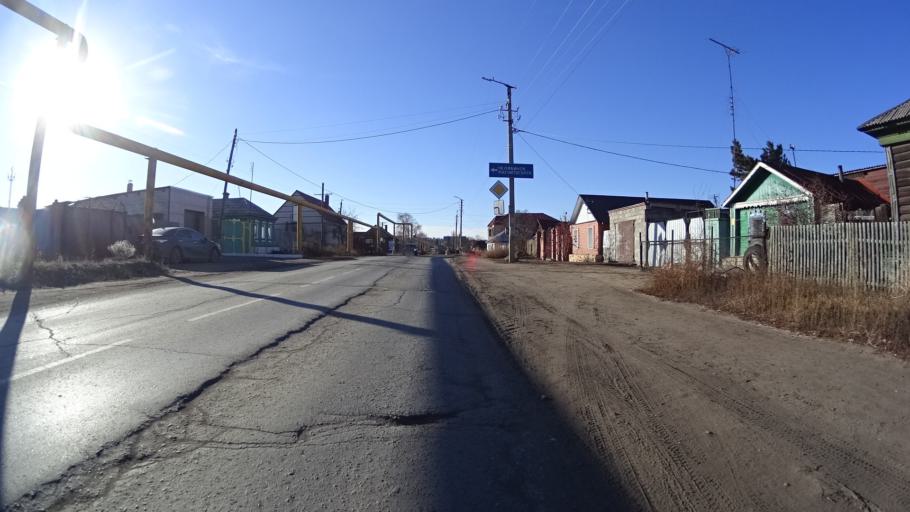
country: RU
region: Chelyabinsk
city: Troitsk
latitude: 54.0916
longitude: 61.5441
